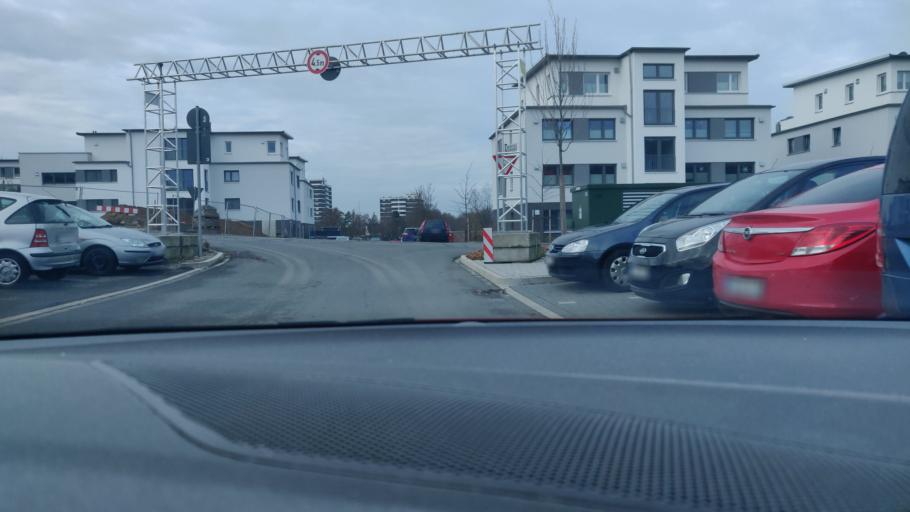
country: DE
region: North Rhine-Westphalia
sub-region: Regierungsbezirk Dusseldorf
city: Heiligenhaus
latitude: 51.3272
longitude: 6.9673
